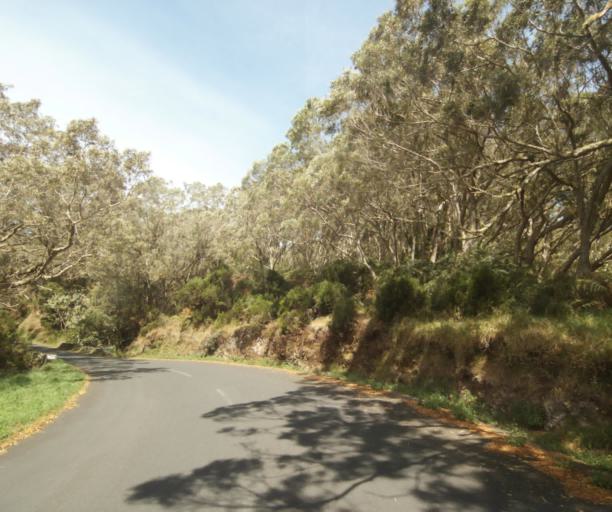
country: RE
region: Reunion
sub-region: Reunion
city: Trois-Bassins
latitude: -21.0564
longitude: 55.3629
